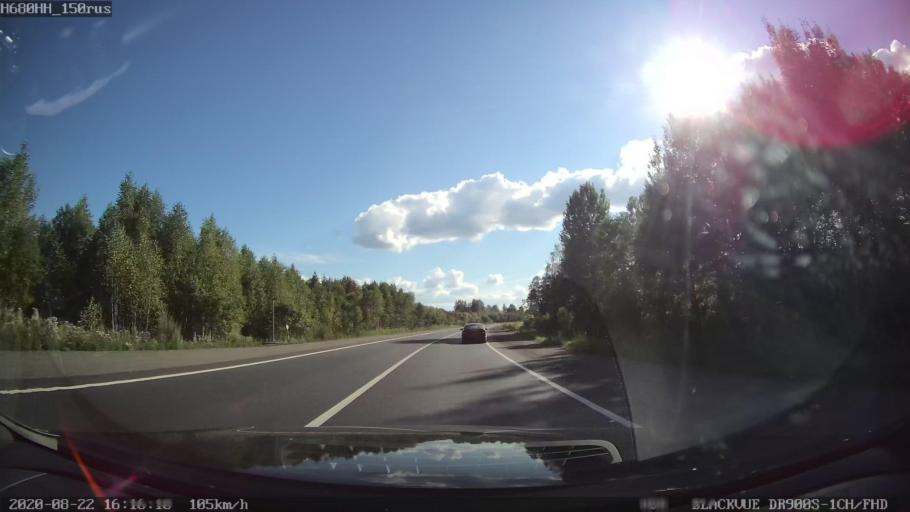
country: RU
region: Tverskaya
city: Rameshki
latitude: 57.4355
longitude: 36.1819
